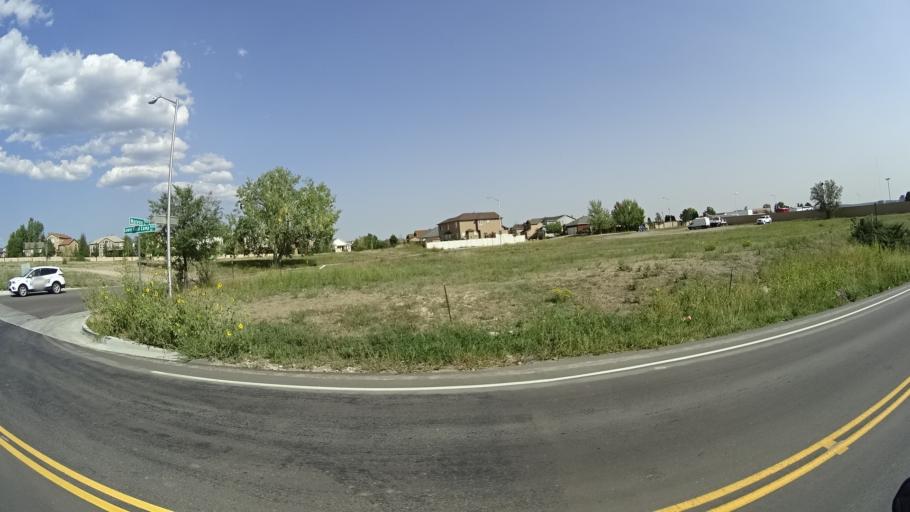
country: US
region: Colorado
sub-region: El Paso County
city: Colorado Springs
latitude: 38.8246
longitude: -104.8488
